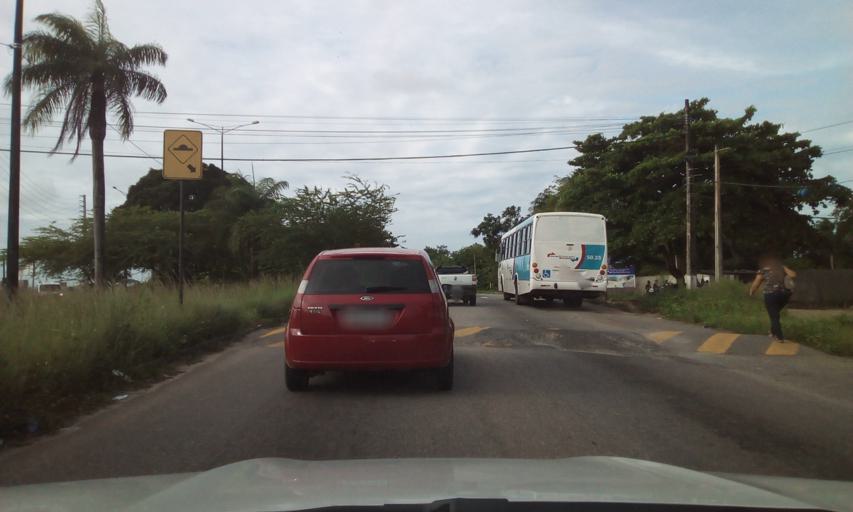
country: BR
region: Paraiba
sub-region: Bayeux
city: Bayeux
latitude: -7.1471
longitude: -34.9086
